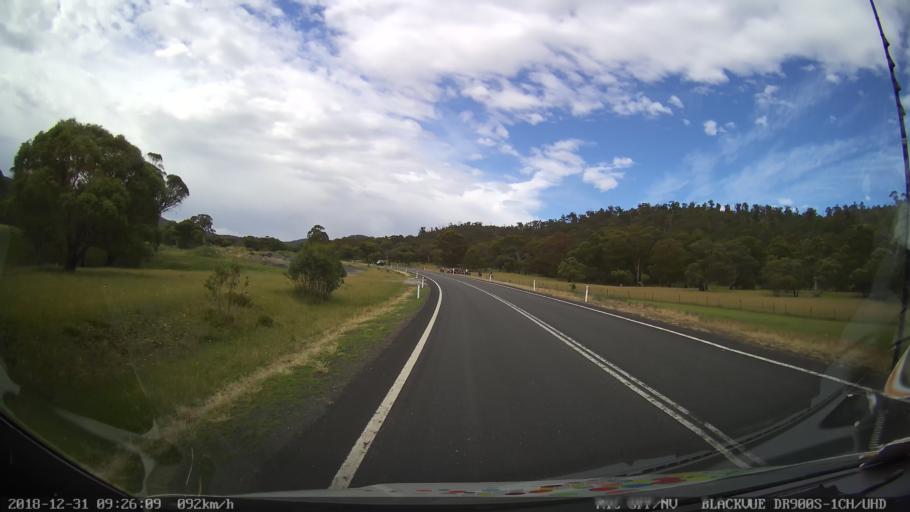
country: AU
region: New South Wales
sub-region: Snowy River
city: Jindabyne
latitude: -36.4439
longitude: 148.4969
